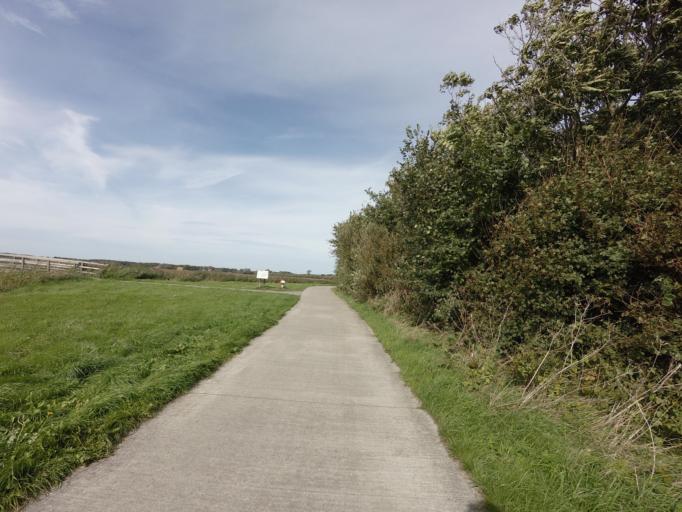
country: NL
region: North Holland
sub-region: Gemeente Texel
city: Den Burg
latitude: 53.0821
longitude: 4.7858
